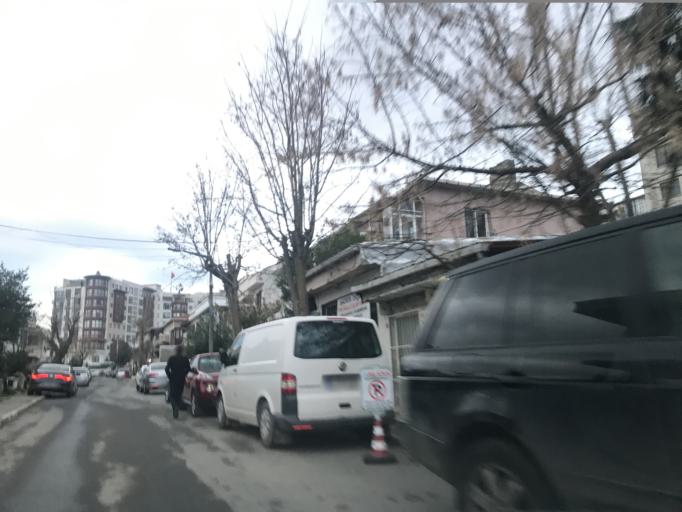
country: TR
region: Istanbul
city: Istanbul
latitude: 41.0410
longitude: 28.9244
